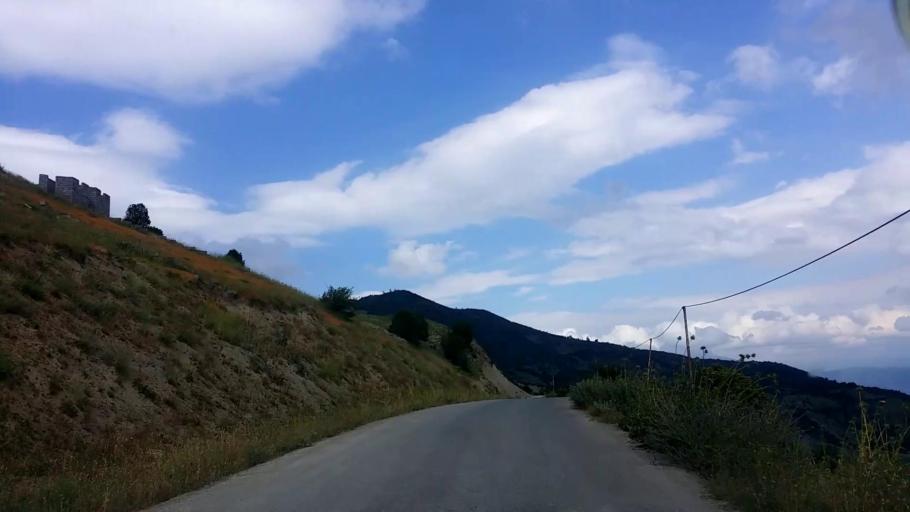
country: IR
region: Mazandaran
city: Chalus
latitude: 36.5528
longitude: 51.2825
